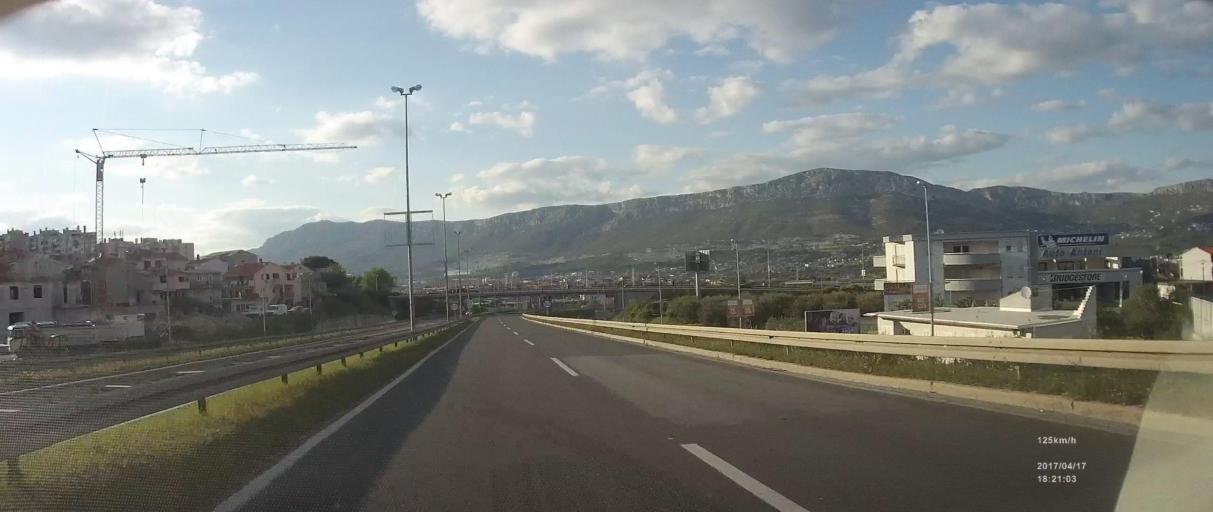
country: HR
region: Splitsko-Dalmatinska
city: Vranjic
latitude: 43.5145
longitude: 16.4824
